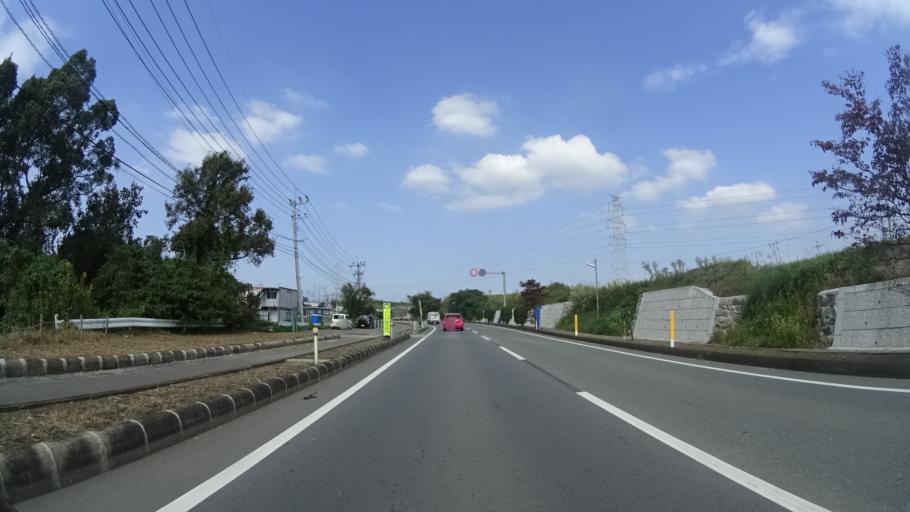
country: JP
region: Kumamoto
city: Ozu
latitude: 32.7933
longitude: 130.8235
